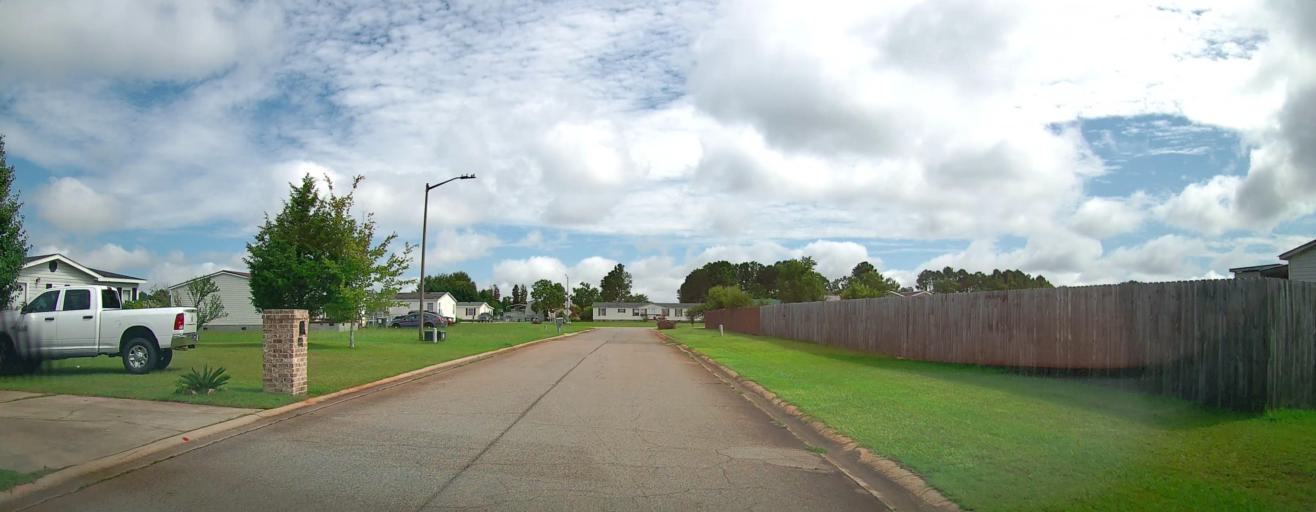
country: US
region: Georgia
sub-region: Houston County
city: Centerville
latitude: 32.6474
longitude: -83.7174
